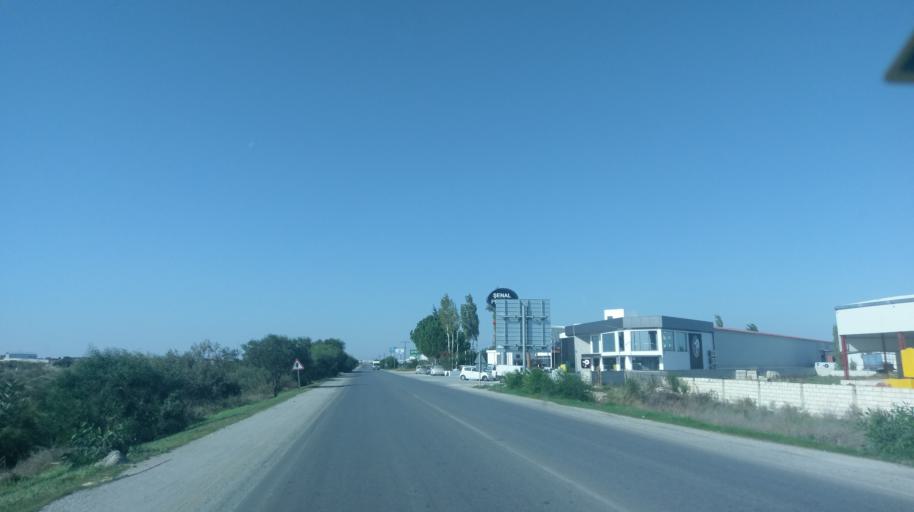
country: CY
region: Ammochostos
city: Famagusta
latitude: 35.1447
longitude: 33.8942
